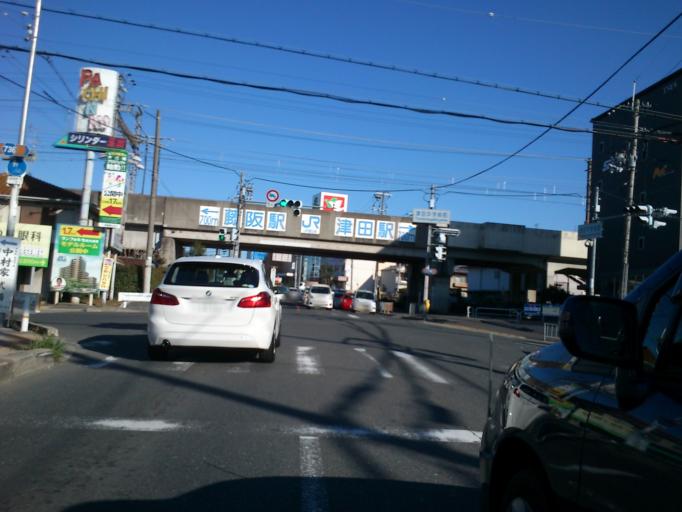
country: JP
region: Osaka
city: Hirakata
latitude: 34.8092
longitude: 135.7001
